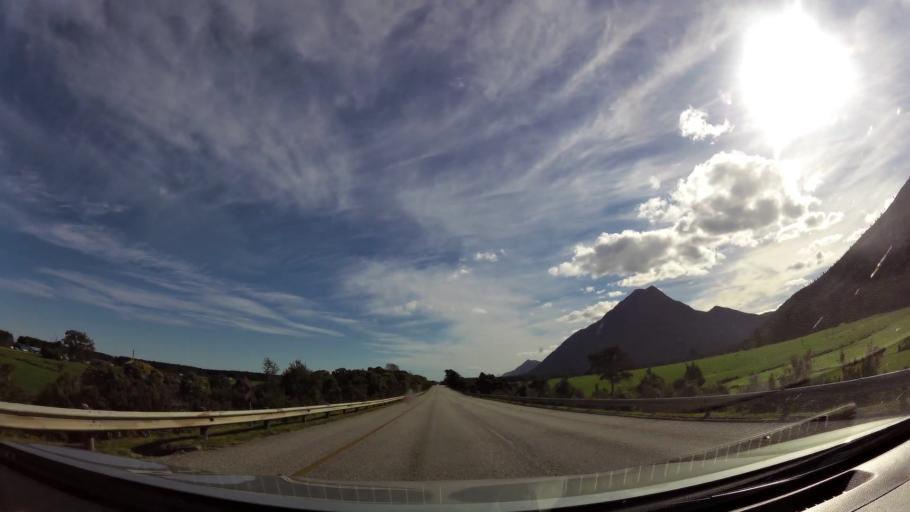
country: ZA
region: Eastern Cape
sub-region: Cacadu District Municipality
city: Kareedouw
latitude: -33.9916
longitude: 24.1455
